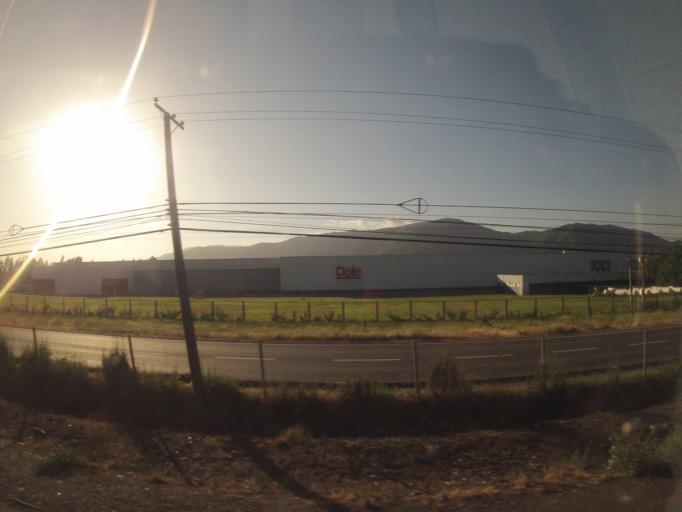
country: CL
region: O'Higgins
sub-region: Provincia de Colchagua
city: Chimbarongo
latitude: -34.5627
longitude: -70.9678
